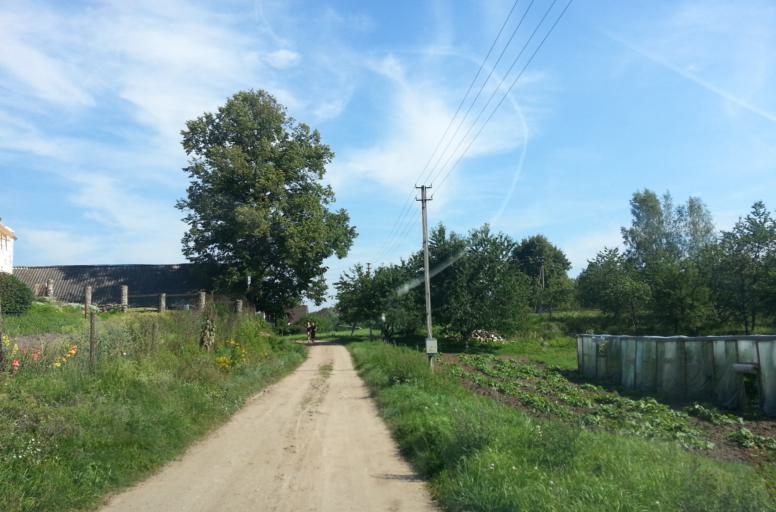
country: LT
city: Grigiskes
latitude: 54.7487
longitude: 25.0231
